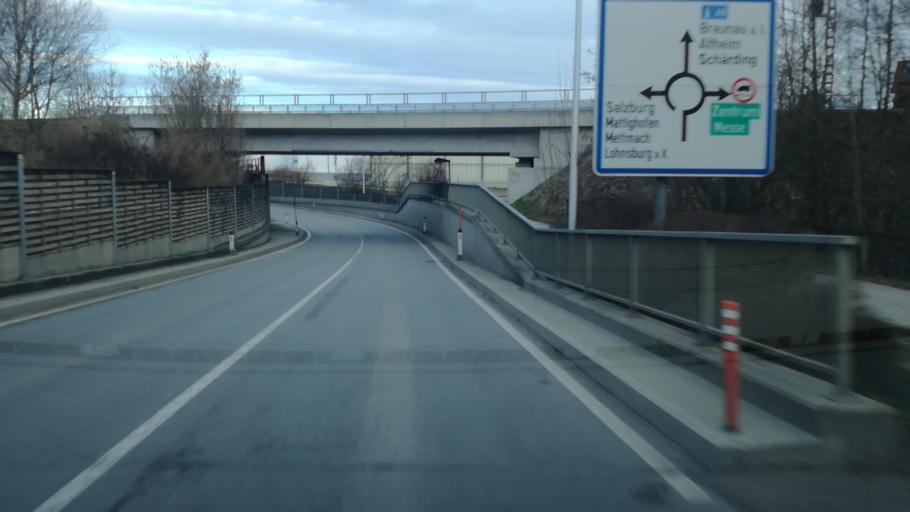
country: AT
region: Upper Austria
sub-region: Politischer Bezirk Ried im Innkreis
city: Ried im Innkreis
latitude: 48.1981
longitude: 13.4751
